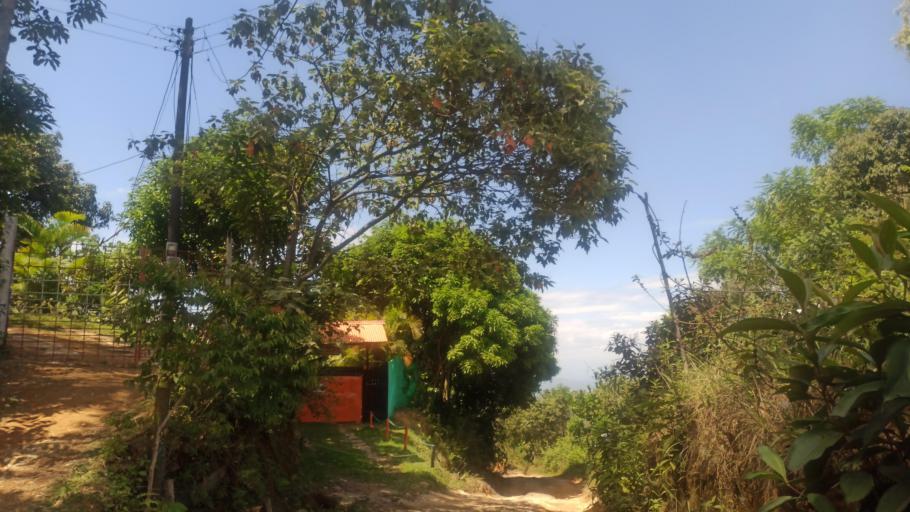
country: CO
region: Valle del Cauca
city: Jamundi
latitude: 3.1878
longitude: -76.6288
